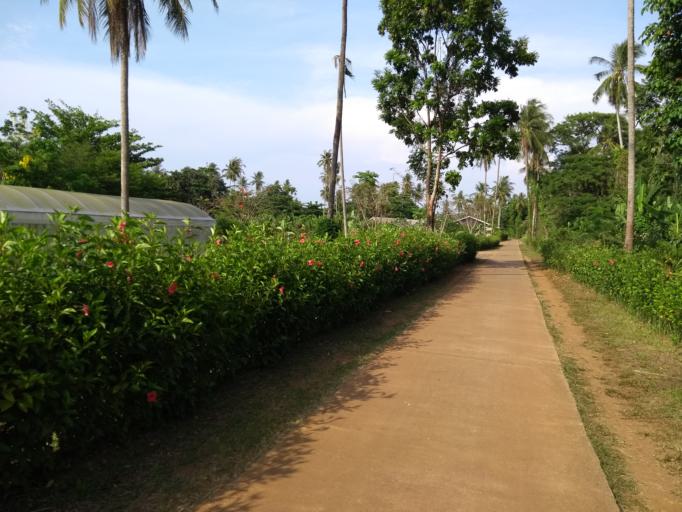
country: TH
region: Trat
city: Ko Kut
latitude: 11.8202
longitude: 102.4668
